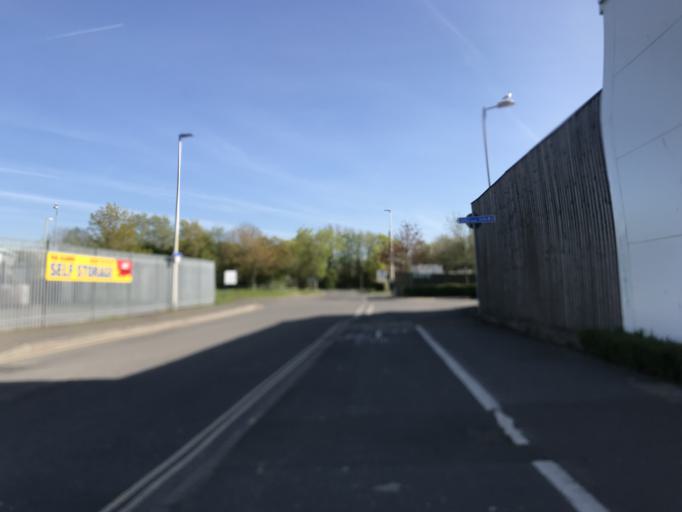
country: GB
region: England
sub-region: Devon
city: Barnstaple
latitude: 51.0728
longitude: -4.0597
